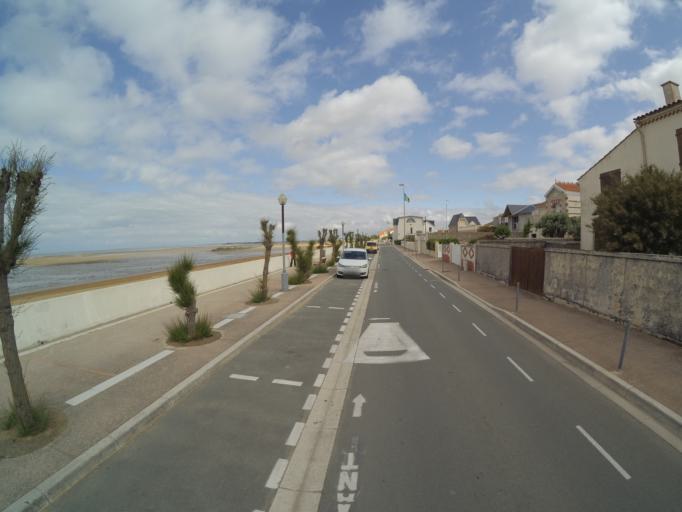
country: FR
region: Poitou-Charentes
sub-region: Departement de la Charente-Maritime
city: Chatelaillon-Plage
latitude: 46.0796
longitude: -1.0949
